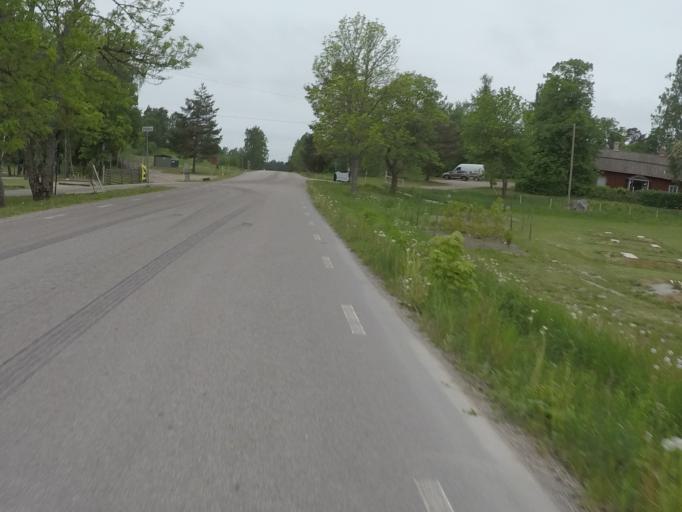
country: SE
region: Vaestmanland
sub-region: Hallstahammars Kommun
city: Kolback
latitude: 59.5457
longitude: 16.2507
